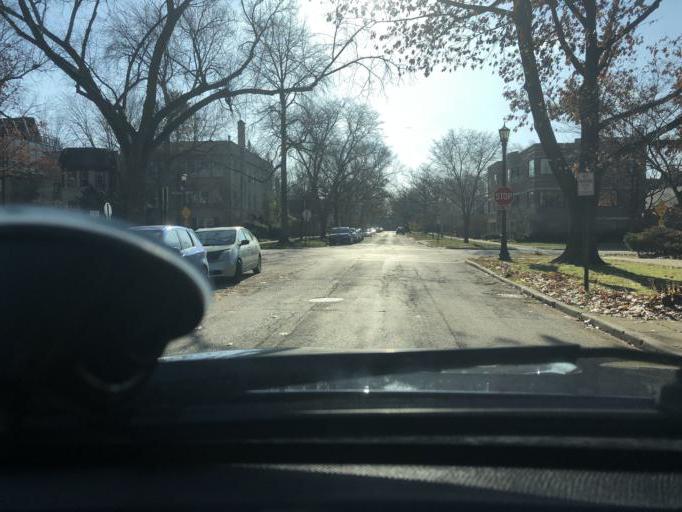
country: US
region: Illinois
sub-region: Cook County
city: Evanston
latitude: 42.0249
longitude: -87.6885
